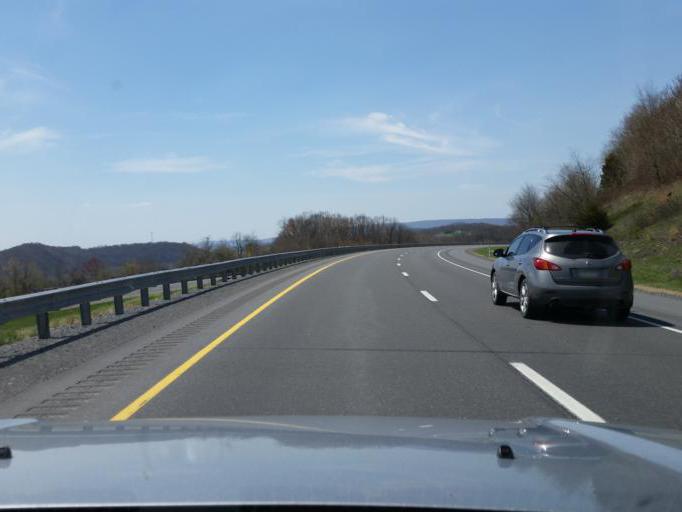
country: US
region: Pennsylvania
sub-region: Juniata County
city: Mifflintown
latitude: 40.5393
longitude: -77.3393
